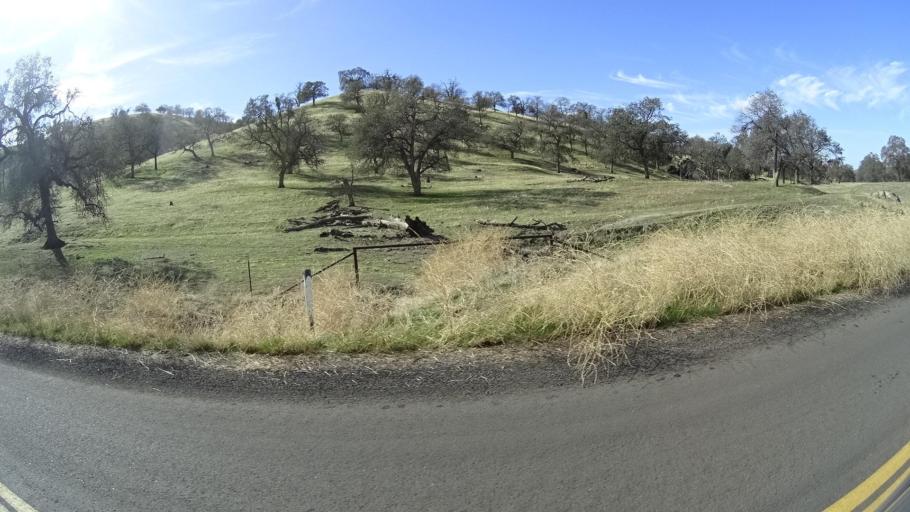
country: US
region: California
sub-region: Tulare County
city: Richgrove
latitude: 35.6710
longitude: -118.8516
